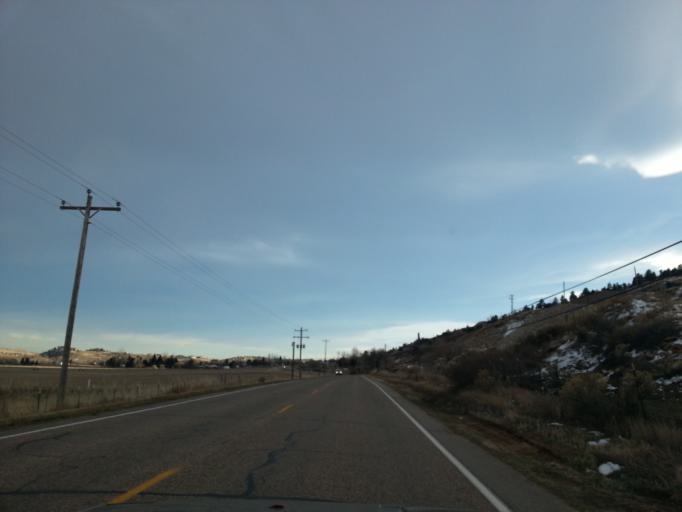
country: US
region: Colorado
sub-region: Larimer County
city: Loveland
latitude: 40.4456
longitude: -105.2023
